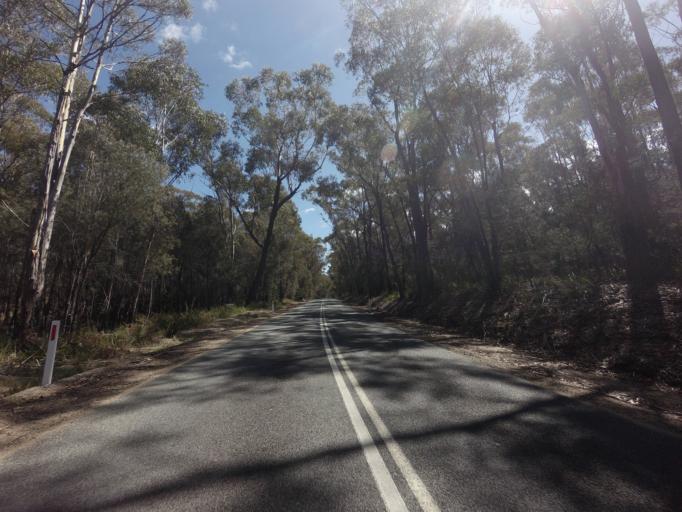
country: AU
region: Tasmania
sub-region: Break O'Day
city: St Helens
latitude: -41.6637
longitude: 148.2807
